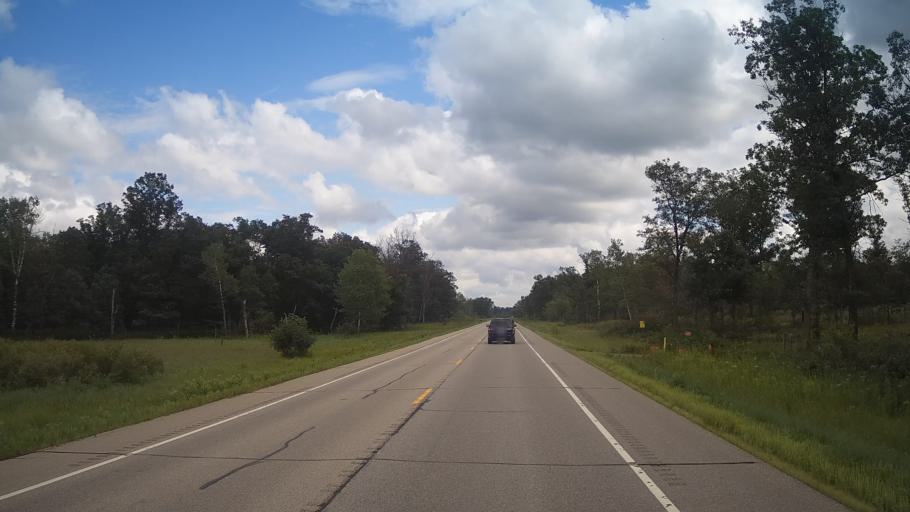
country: US
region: Wisconsin
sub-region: Adams County
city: Friendship
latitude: 44.0257
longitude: -89.7014
